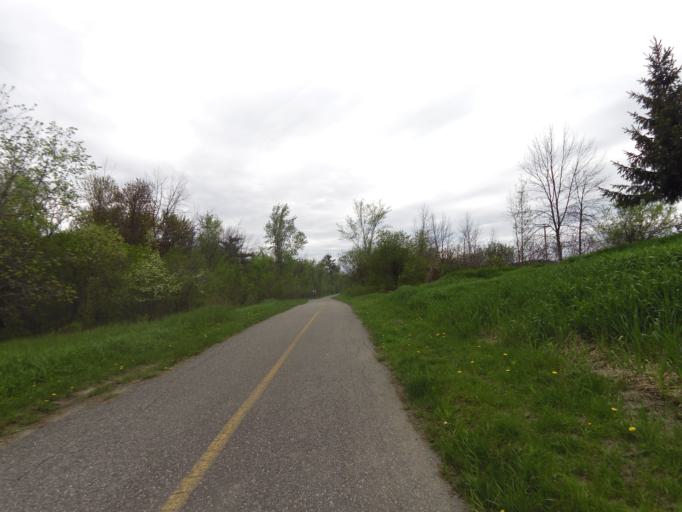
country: CA
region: Quebec
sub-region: Outaouais
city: Gatineau
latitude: 45.4671
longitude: -75.7319
